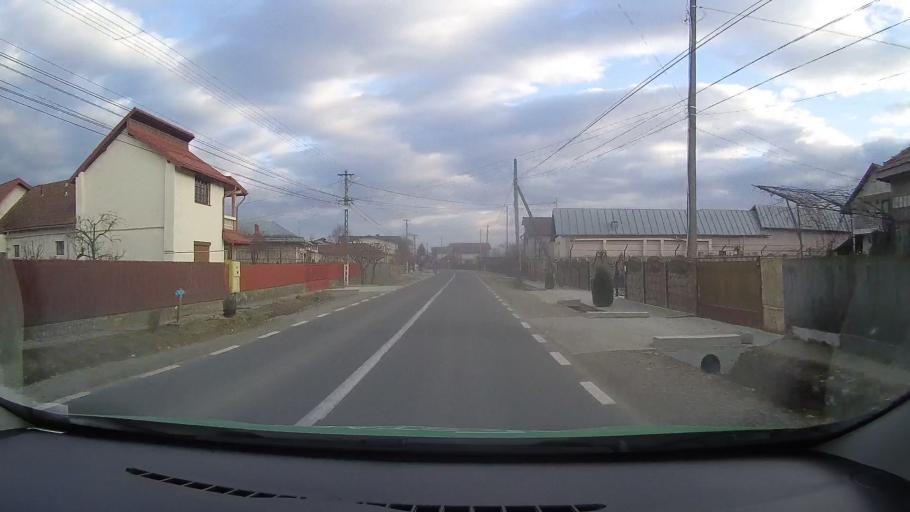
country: RO
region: Dambovita
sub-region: Comuna I. L. Caragiale
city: Ghirdoveni
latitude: 44.9360
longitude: 25.6831
